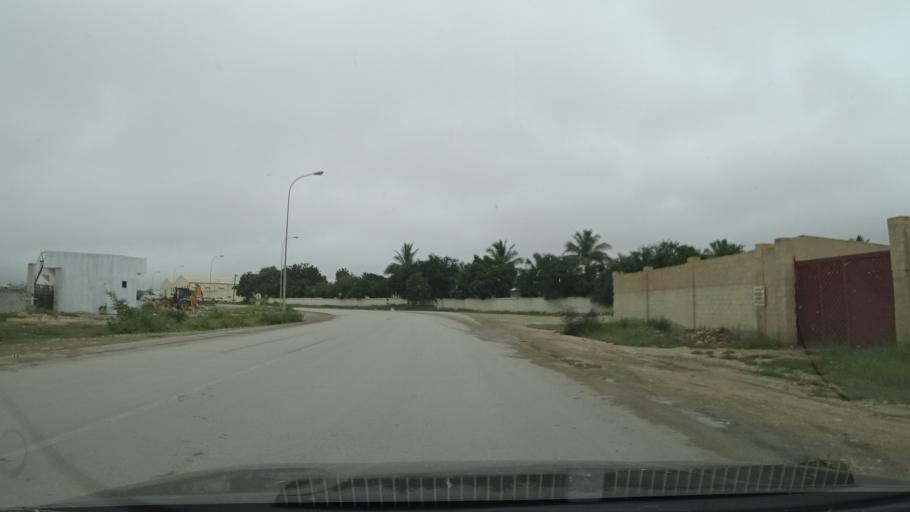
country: OM
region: Zufar
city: Salalah
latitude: 17.0124
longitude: 54.0444
